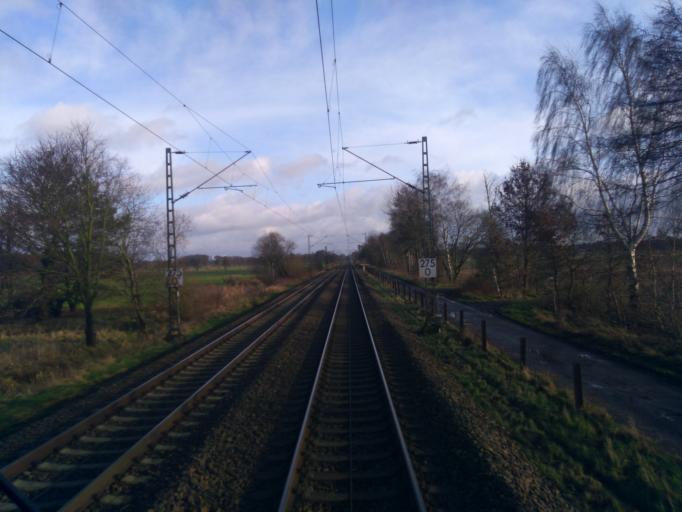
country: DE
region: Lower Saxony
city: Hassendorf
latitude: 53.1019
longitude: 9.2809
